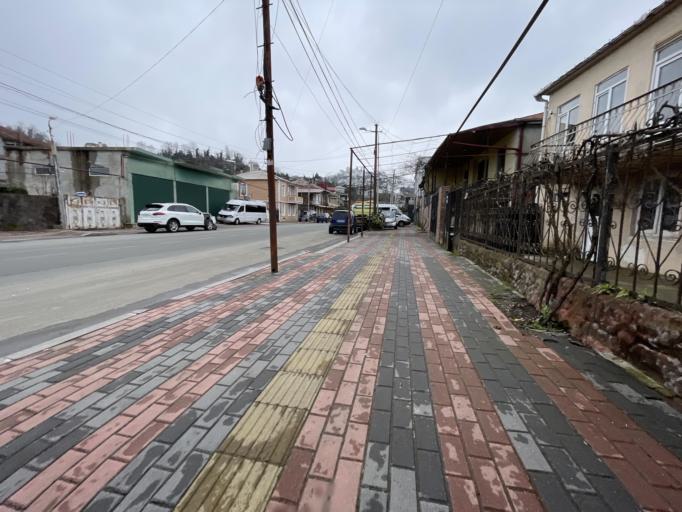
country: GE
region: Ajaria
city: Batumi
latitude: 41.6353
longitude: 41.6434
